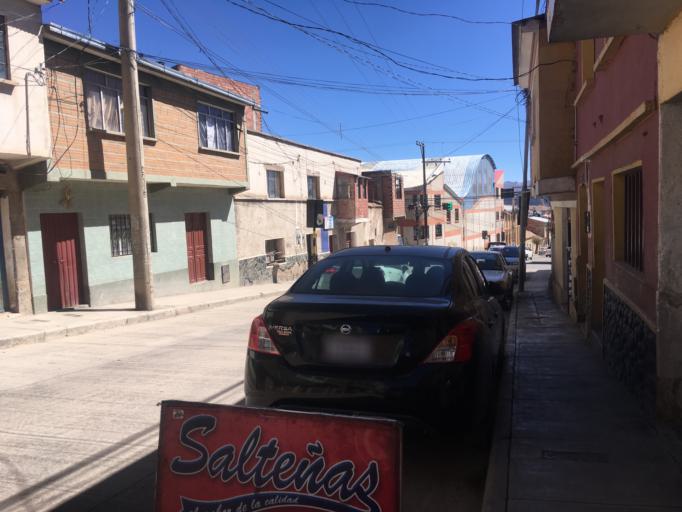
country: BO
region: Potosi
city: Potosi
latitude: -19.5813
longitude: -65.7558
